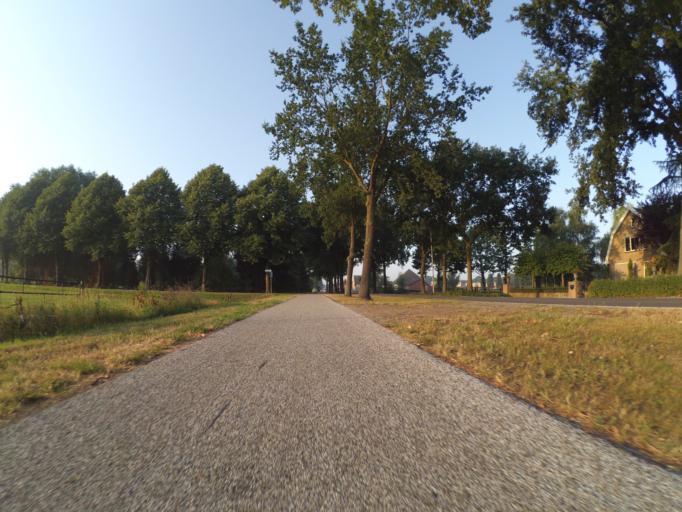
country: NL
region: Overijssel
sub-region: Gemeente Twenterand
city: Vriezenveen
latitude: 52.4177
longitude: 6.6276
